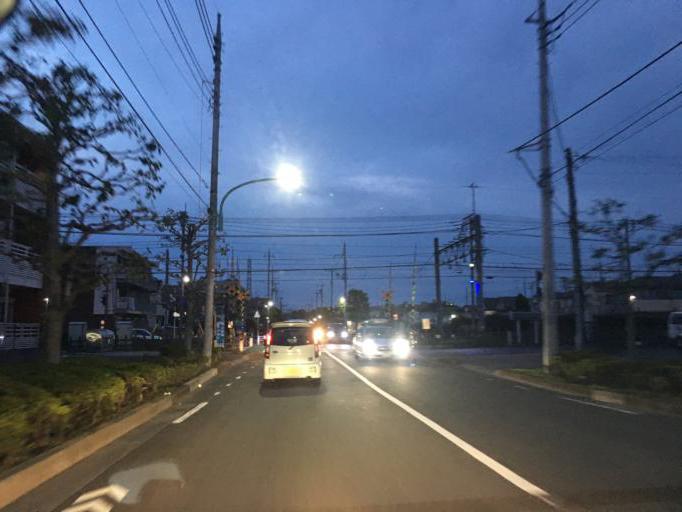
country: JP
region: Tokyo
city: Higashimurayama-shi
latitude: 35.7326
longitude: 139.4527
